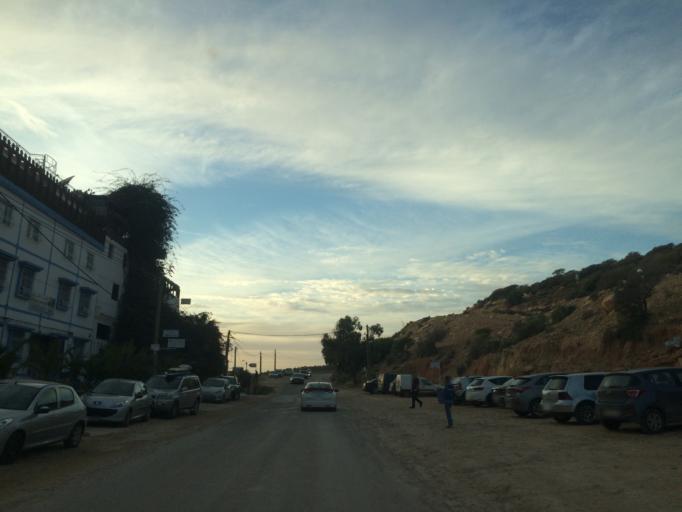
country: MA
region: Souss-Massa-Draa
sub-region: Agadir-Ida-ou-Tnan
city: Taghazout
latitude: 30.5459
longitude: -9.7129
